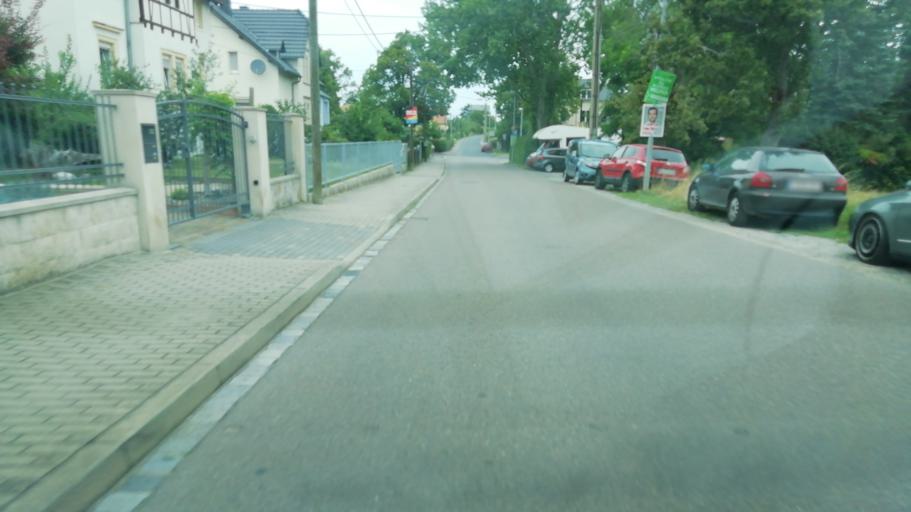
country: DE
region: Saxony
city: Coswig
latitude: 51.0801
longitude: 13.6029
